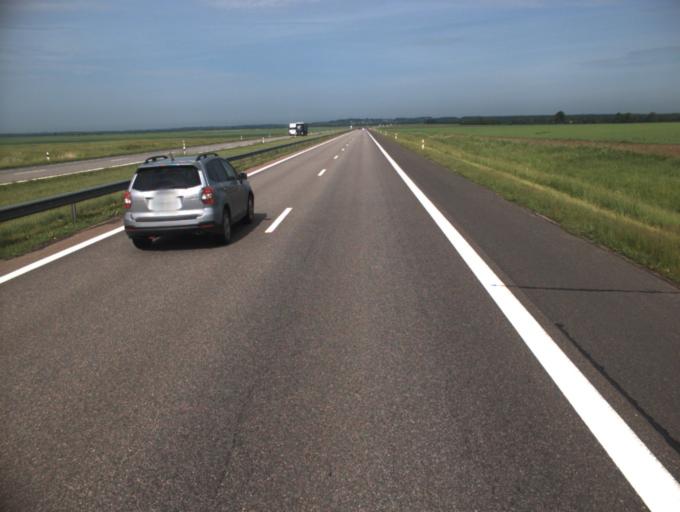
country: LT
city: Raseiniai
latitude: 55.3230
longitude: 23.1846
